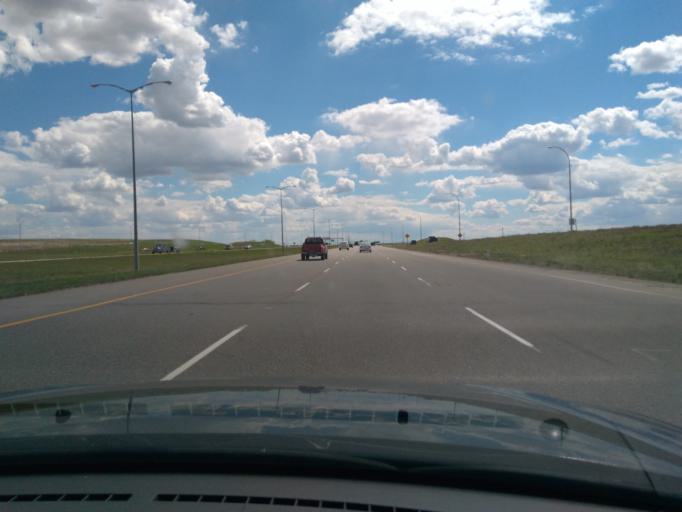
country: CA
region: Alberta
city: Chestermere
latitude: 51.0362
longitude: -113.9216
